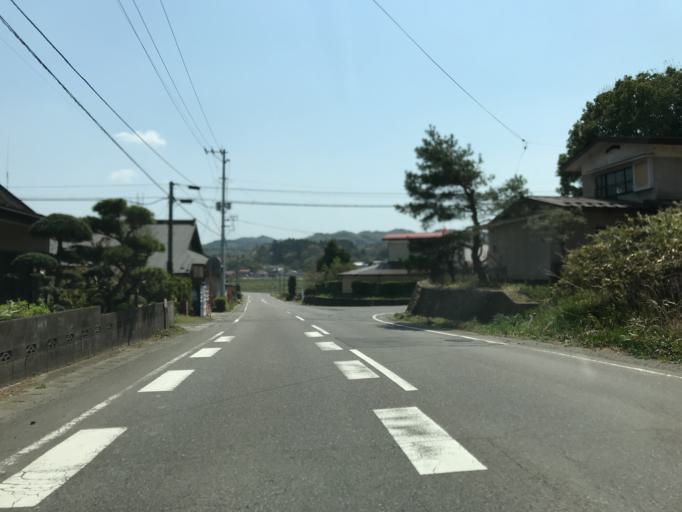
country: JP
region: Fukushima
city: Ishikawa
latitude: 37.0708
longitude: 140.4241
